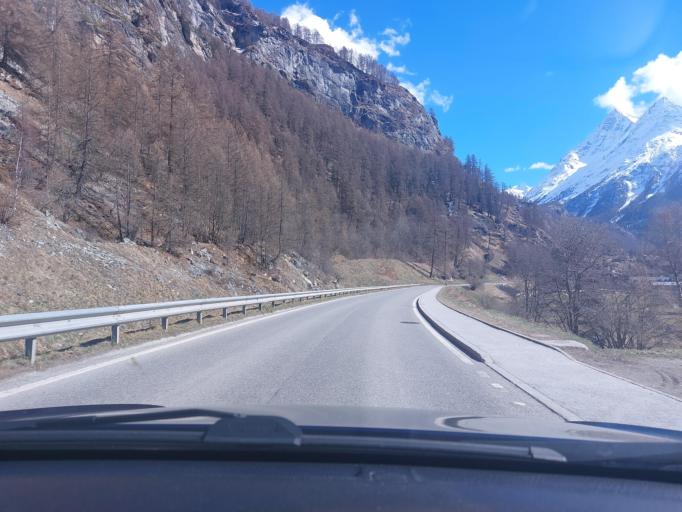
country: CH
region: Valais
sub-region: Herens District
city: Evolene
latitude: 46.1138
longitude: 7.4981
